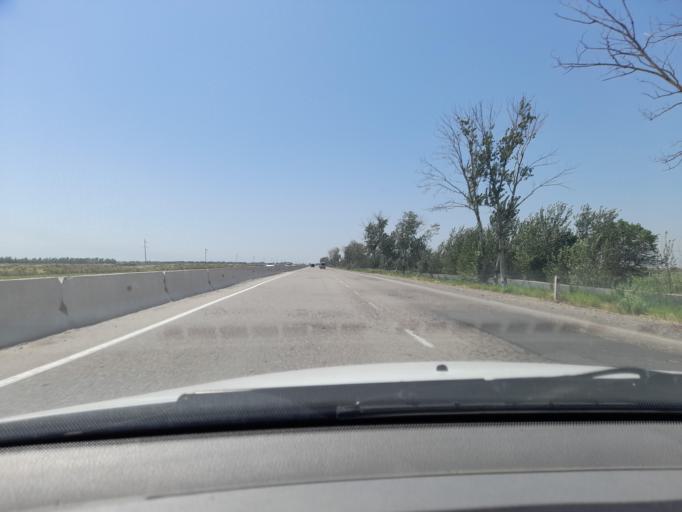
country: UZ
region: Jizzax
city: Dustlik
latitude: 40.3923
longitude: 68.1797
